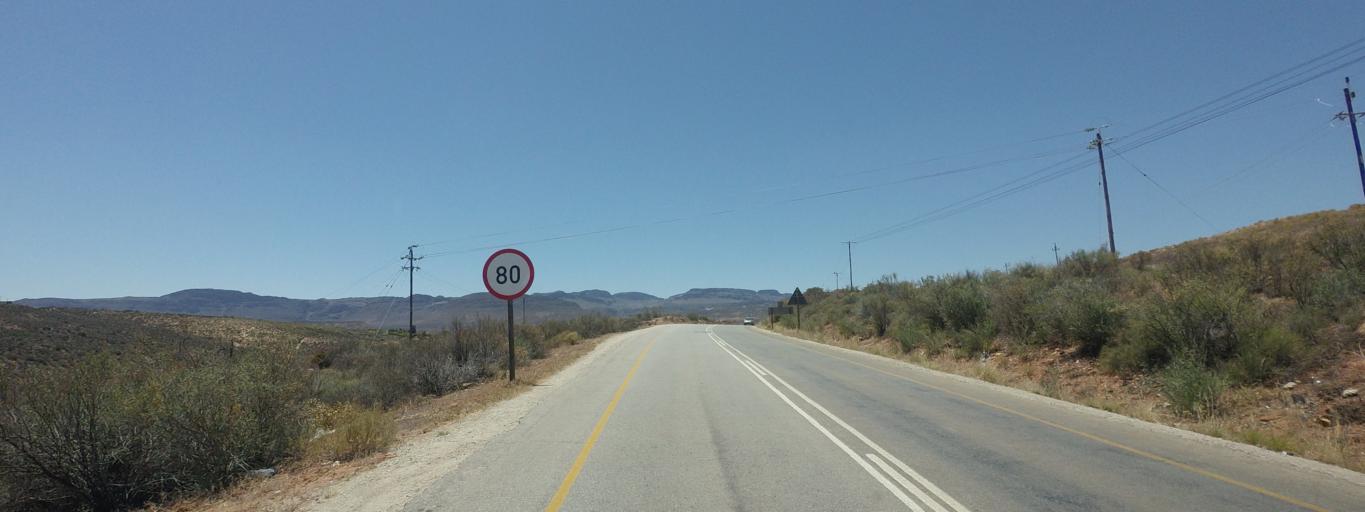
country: ZA
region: Western Cape
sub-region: West Coast District Municipality
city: Clanwilliam
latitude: -32.1713
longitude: 18.8731
